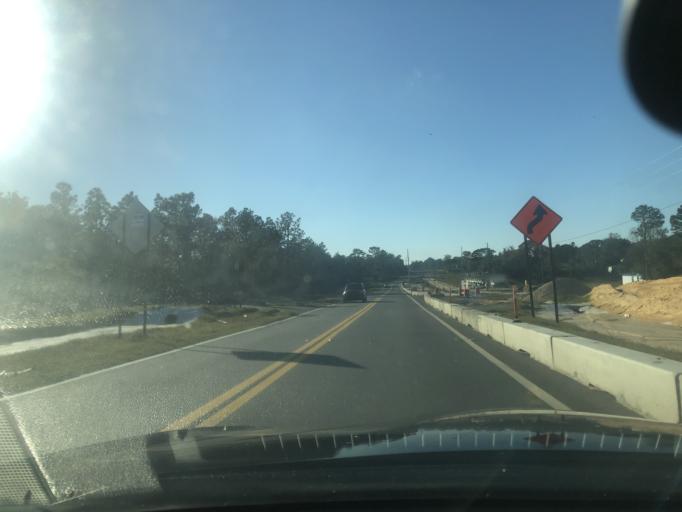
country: US
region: Florida
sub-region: Citrus County
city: Sugarmill Woods
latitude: 28.7639
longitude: -82.5030
